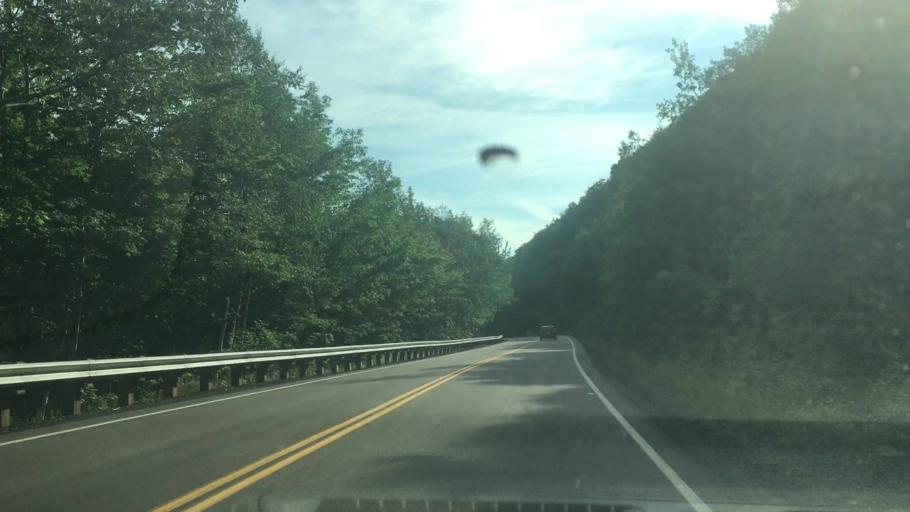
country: CA
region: Nova Scotia
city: Sydney Mines
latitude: 46.8244
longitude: -60.6254
